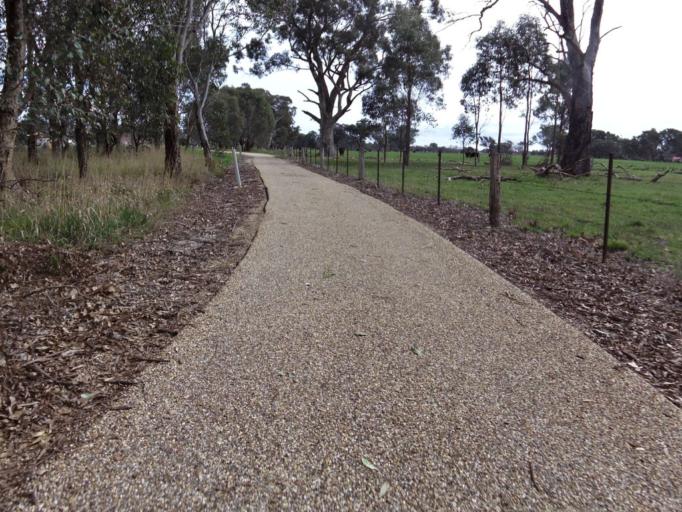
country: AU
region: Victoria
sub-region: Wangaratta
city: Wangaratta
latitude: -36.3919
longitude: 146.3373
